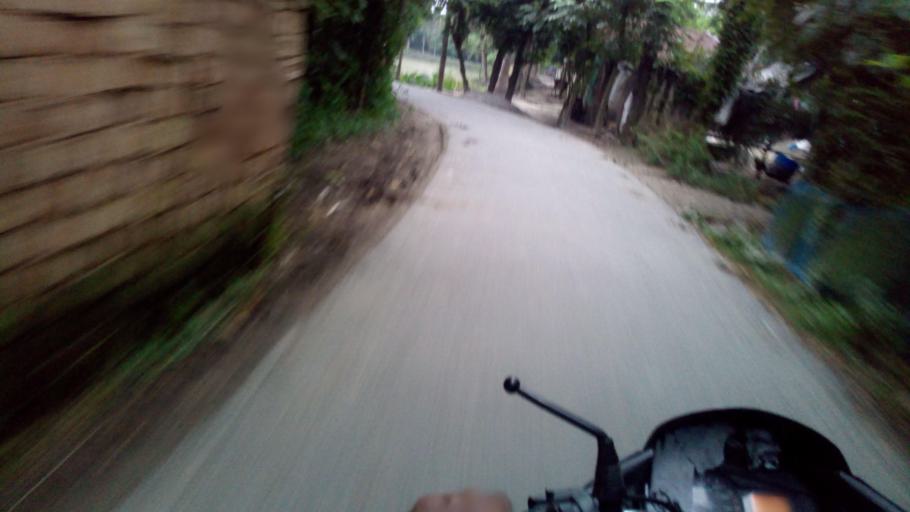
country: BD
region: Khulna
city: Phultala
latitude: 22.7625
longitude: 89.4086
